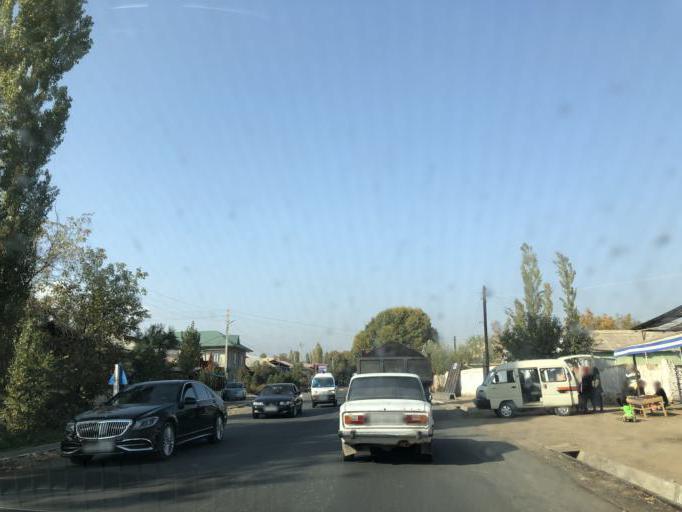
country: UZ
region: Namangan
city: Chust Shahri
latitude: 41.0713
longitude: 71.2046
